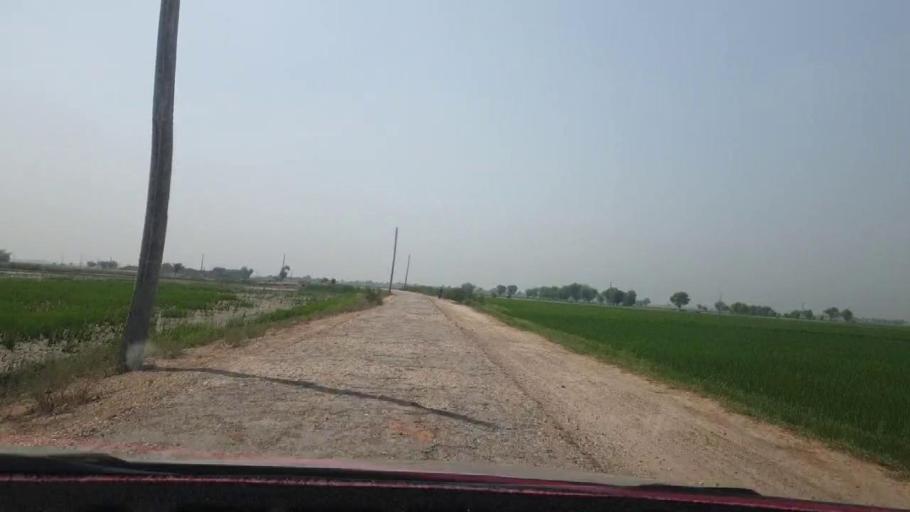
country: PK
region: Sindh
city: Warah
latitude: 27.4086
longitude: 67.8447
